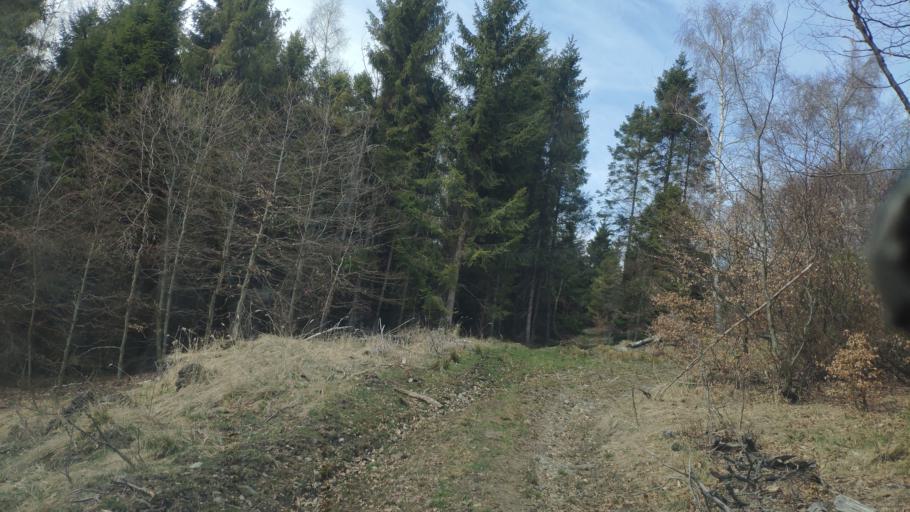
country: SK
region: Kosicky
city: Gelnica
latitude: 48.7606
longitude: 21.0166
